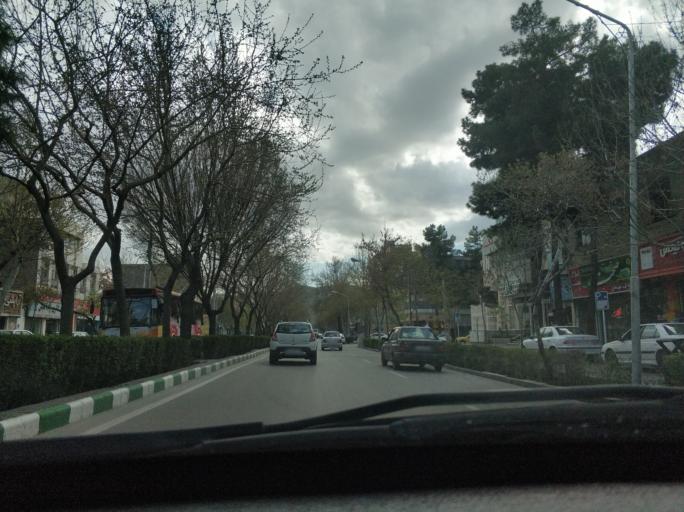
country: IR
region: Razavi Khorasan
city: Mashhad
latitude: 36.2728
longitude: 59.5906
